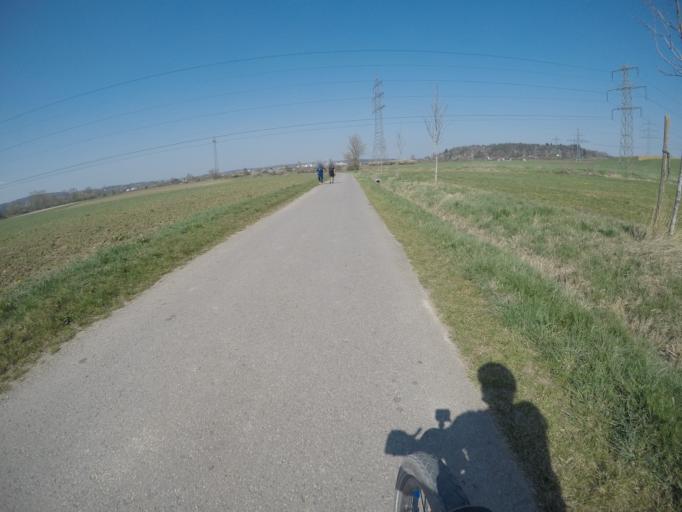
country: DE
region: Baden-Wuerttemberg
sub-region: Regierungsbezirk Stuttgart
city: Renningen
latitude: 48.7660
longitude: 8.9590
